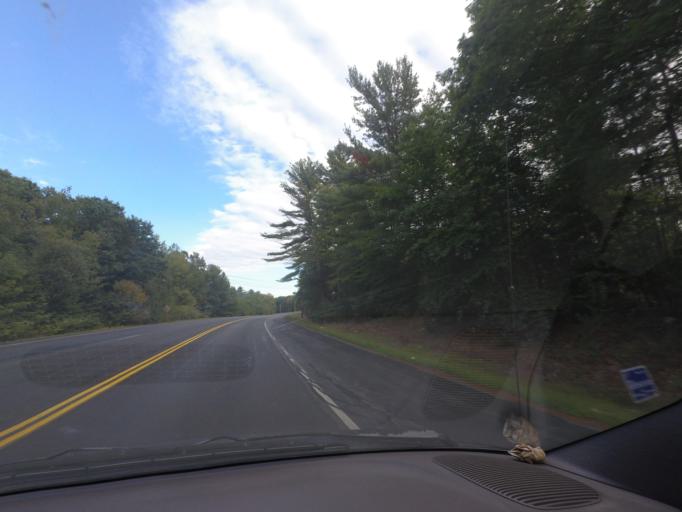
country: US
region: Maine
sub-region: York County
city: Sanford (historical)
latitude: 43.4305
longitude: -70.8023
